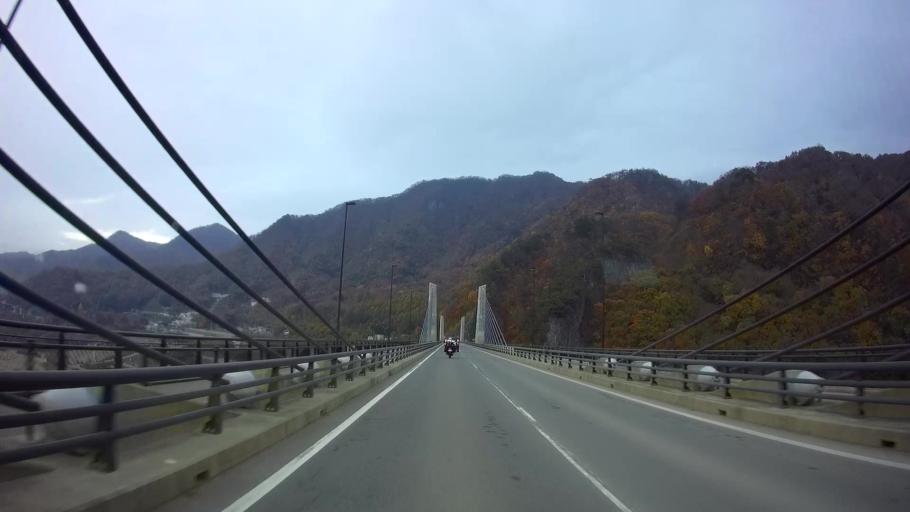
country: JP
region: Gunma
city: Nakanojomachi
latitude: 36.5457
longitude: 138.6869
